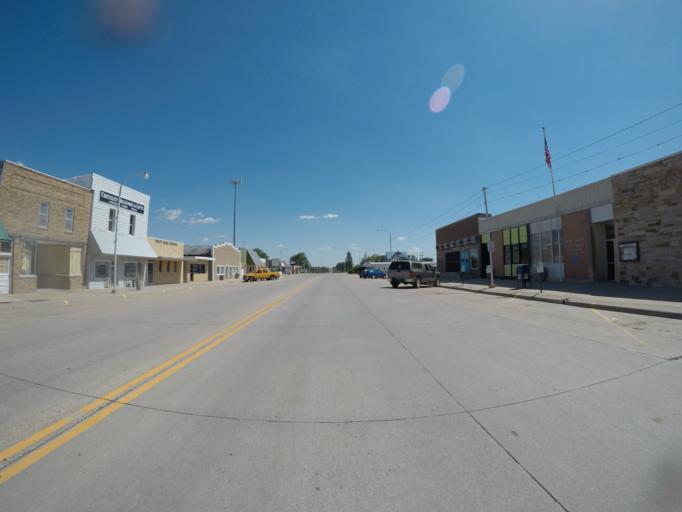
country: US
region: Kansas
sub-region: Sheridan County
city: Hoxie
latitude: 39.3536
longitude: -100.4420
